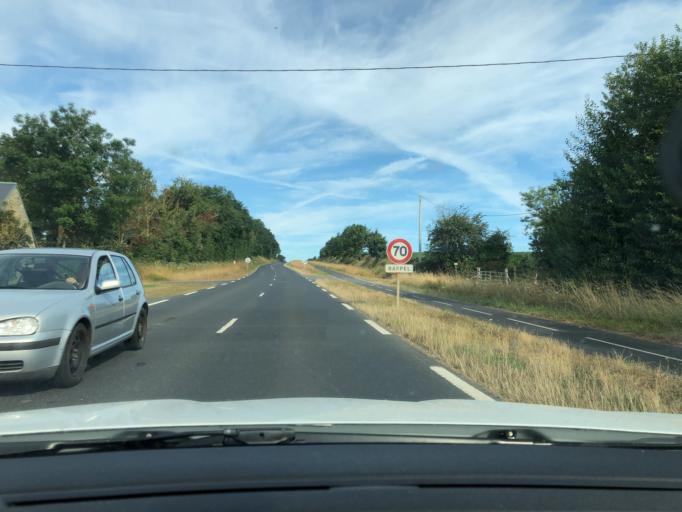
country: FR
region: Lower Normandy
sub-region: Departement du Calvados
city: Saint-Vigor-le-Grand
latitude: 49.2523
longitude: -0.6352
